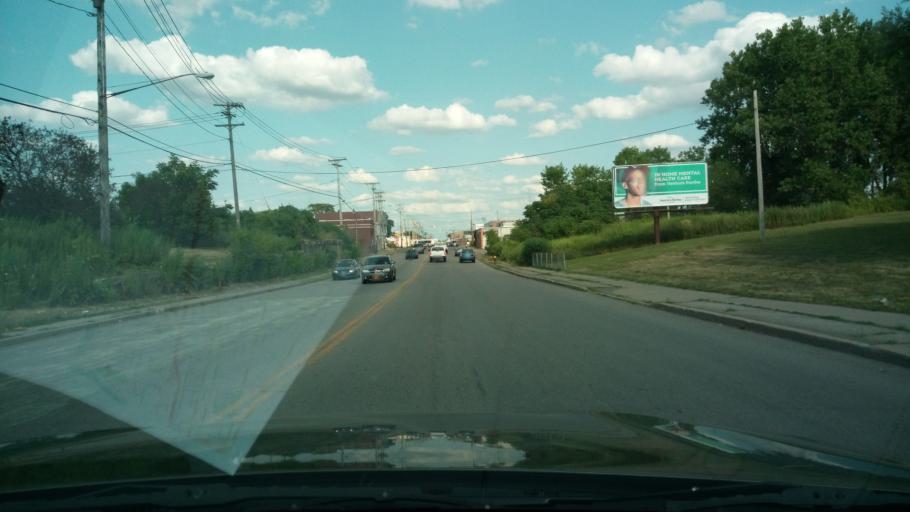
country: US
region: New York
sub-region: Erie County
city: Sloan
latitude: 42.8848
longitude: -78.8174
